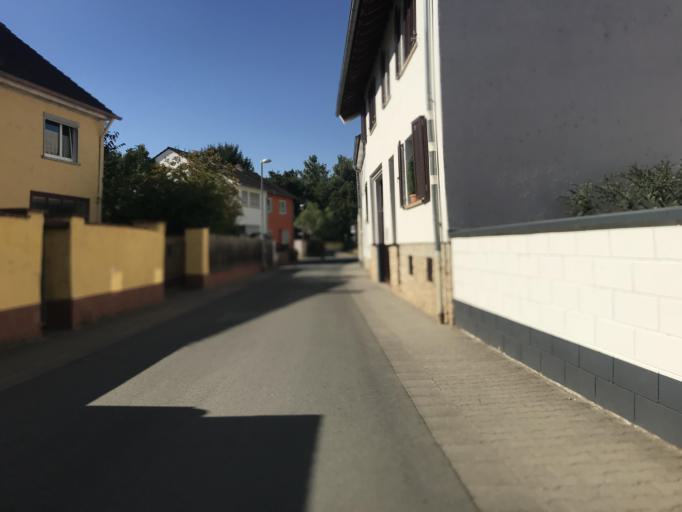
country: DE
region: Rheinland-Pfalz
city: Oestrich-Winkel
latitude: 49.9924
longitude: 8.0275
